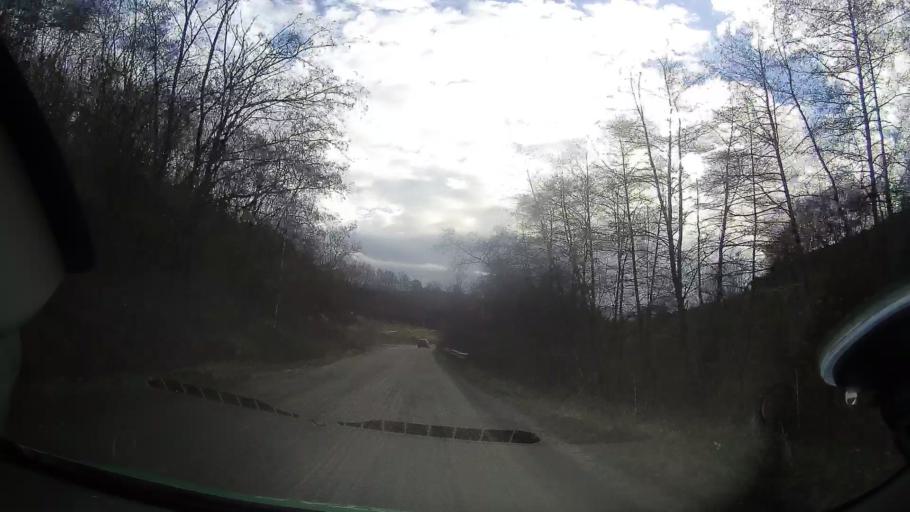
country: RO
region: Cluj
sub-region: Comuna Baisoara
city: Baisoara
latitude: 46.5844
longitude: 23.4614
